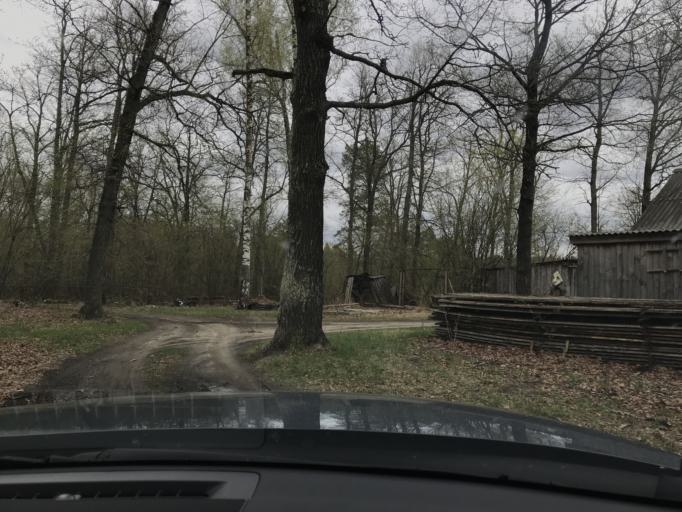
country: RU
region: Mordoviya
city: Shiringushi
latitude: 53.8551
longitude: 42.7844
